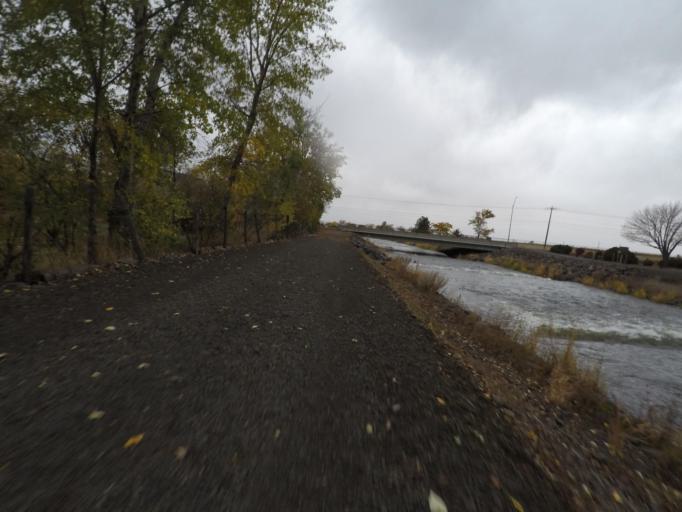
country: US
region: Washington
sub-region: Walla Walla County
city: Walla Walla East
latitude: 46.0762
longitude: -118.2828
